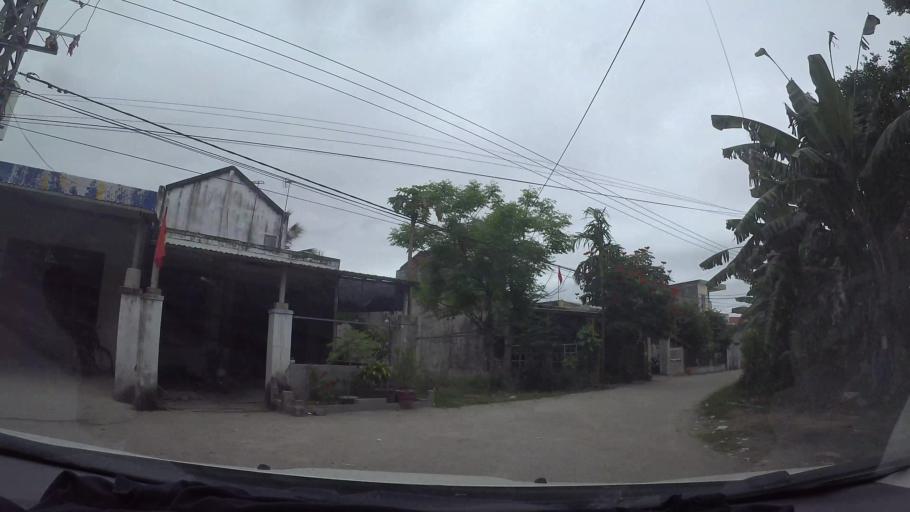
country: VN
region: Da Nang
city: Lien Chieu
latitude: 16.0898
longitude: 108.1024
